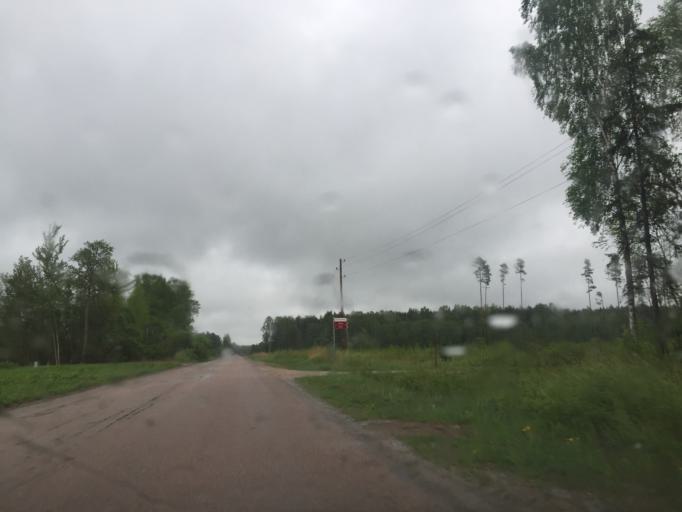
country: LV
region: Ogre
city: Jumprava
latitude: 56.6530
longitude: 24.9308
